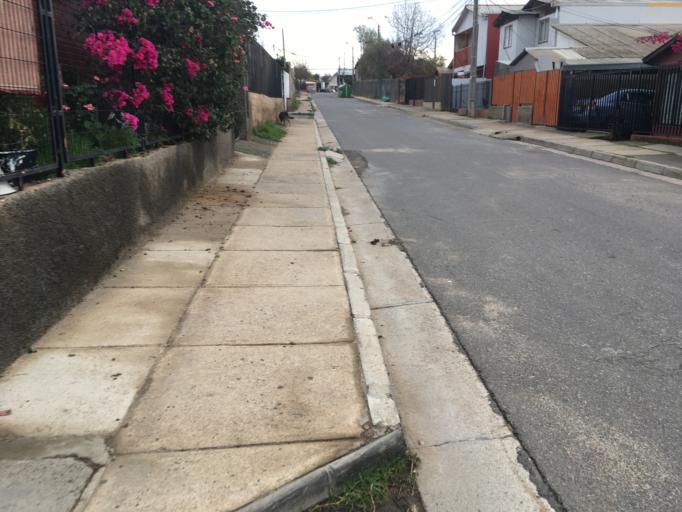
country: CL
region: Valparaiso
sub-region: Provincia de Valparaiso
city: Vina del Mar
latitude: -33.0044
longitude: -71.4957
